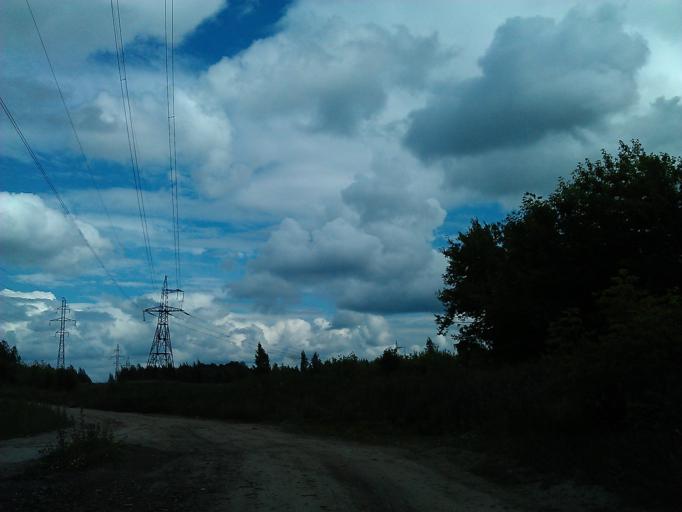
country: LV
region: Riga
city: Jaunciems
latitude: 56.9917
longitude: 24.1950
